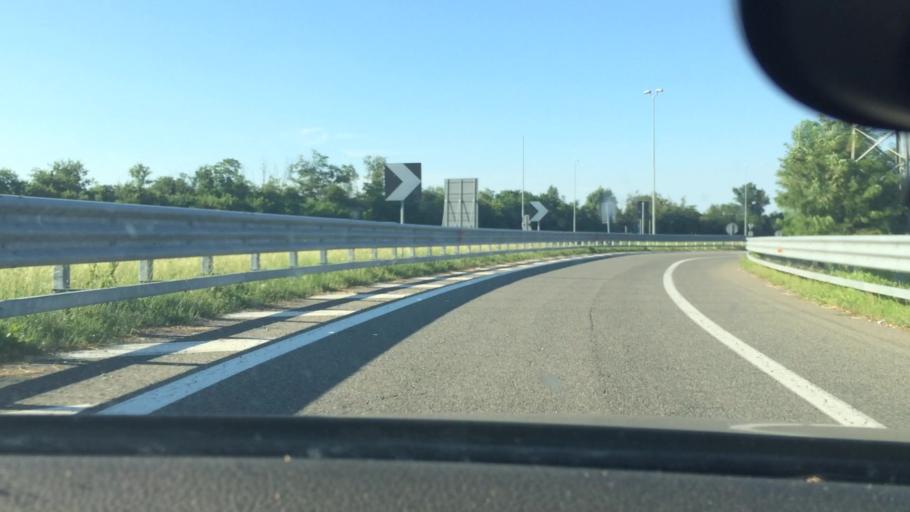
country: IT
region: Lombardy
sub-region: Citta metropolitana di Milano
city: Cerro Maggiore
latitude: 45.6042
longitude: 8.9478
